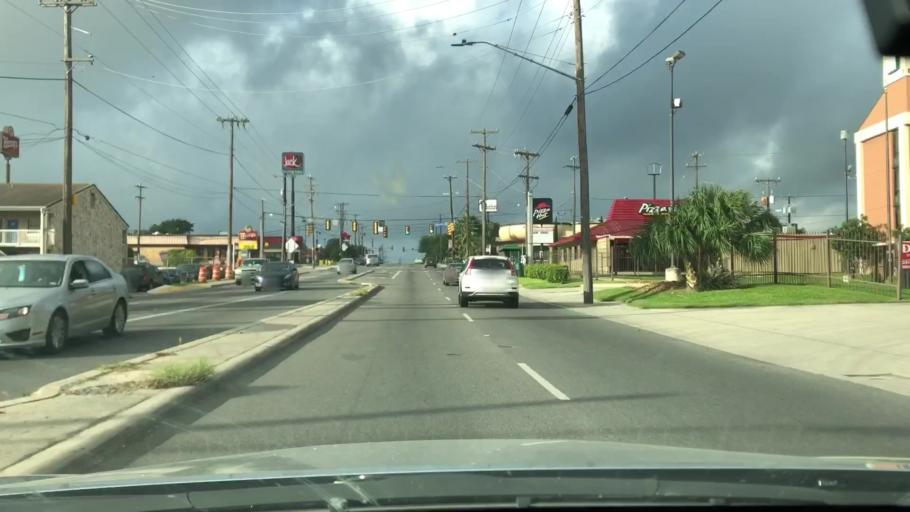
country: US
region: Texas
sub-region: Bexar County
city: Balcones Heights
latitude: 29.5304
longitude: -98.5630
